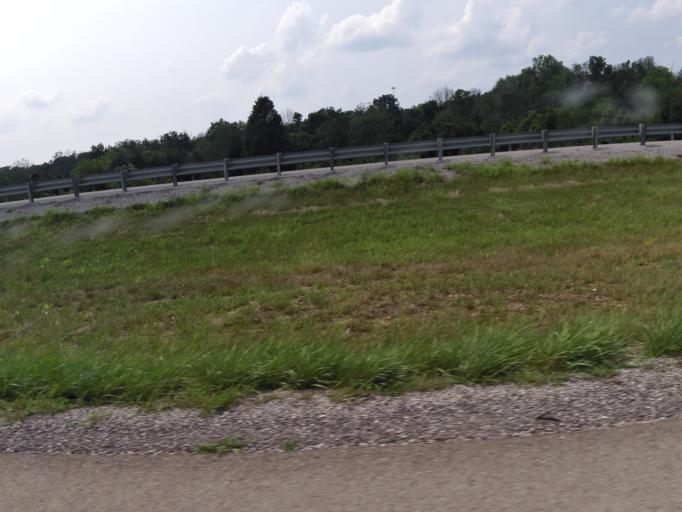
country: US
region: Kentucky
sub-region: Boone County
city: Walton
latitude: 38.8784
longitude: -84.6229
